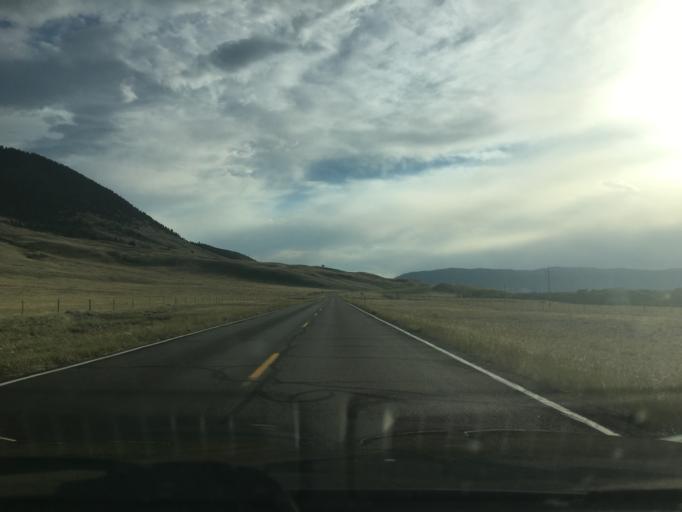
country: US
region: Wyoming
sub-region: Albany County
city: Laramie
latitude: 41.2883
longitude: -106.0368
